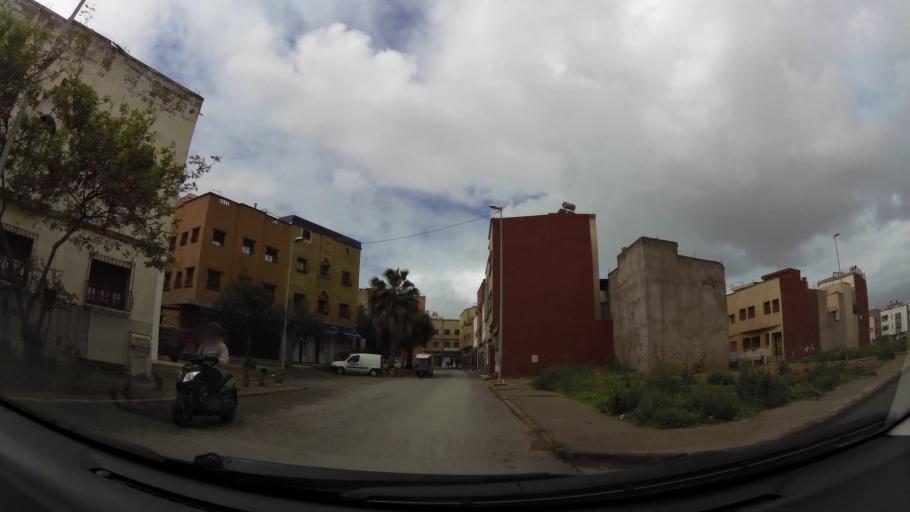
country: MA
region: Grand Casablanca
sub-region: Casablanca
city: Casablanca
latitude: 33.5661
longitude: -7.6901
